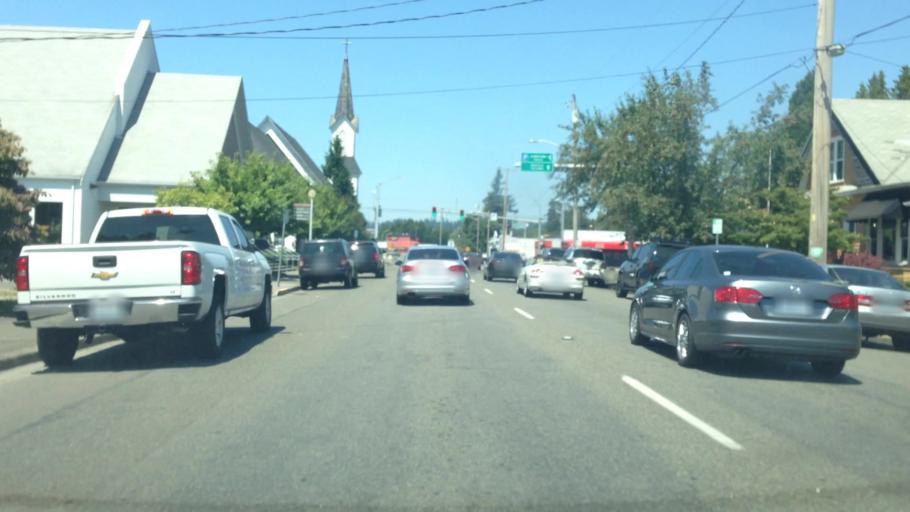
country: US
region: Washington
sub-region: Pierce County
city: Puyallup
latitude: 47.1894
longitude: -122.2913
